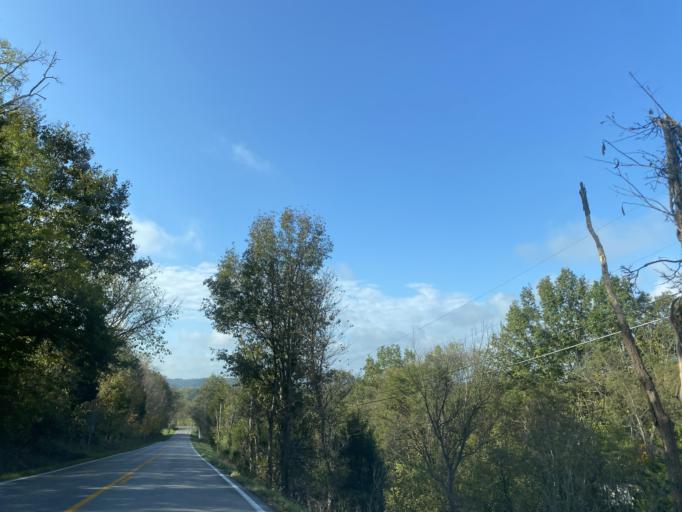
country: US
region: Kentucky
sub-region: Pendleton County
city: Falmouth
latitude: 38.6816
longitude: -84.3199
